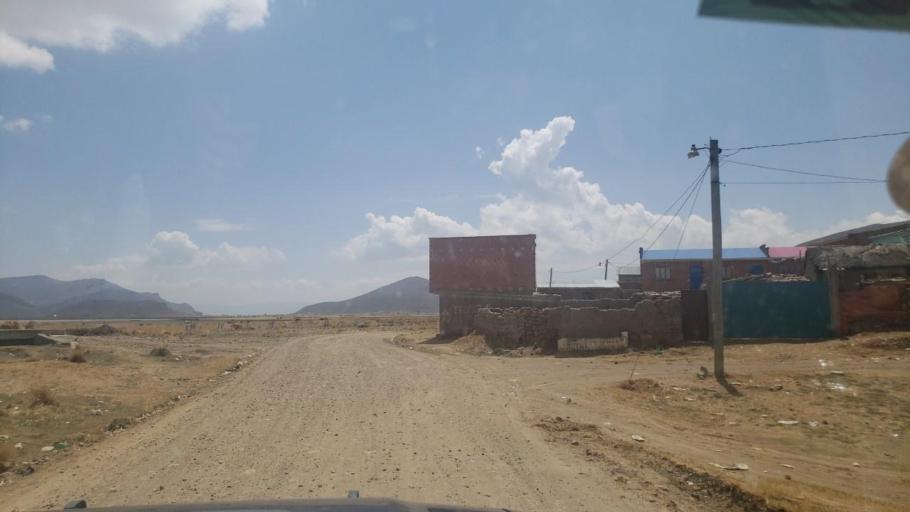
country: BO
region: La Paz
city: Batallas
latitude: -16.3862
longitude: -68.5971
